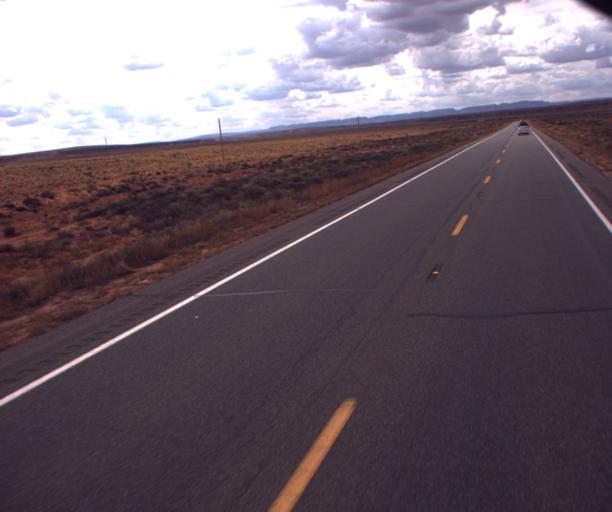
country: US
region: Arizona
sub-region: Navajo County
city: Kayenta
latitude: 36.7902
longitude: -109.9495
